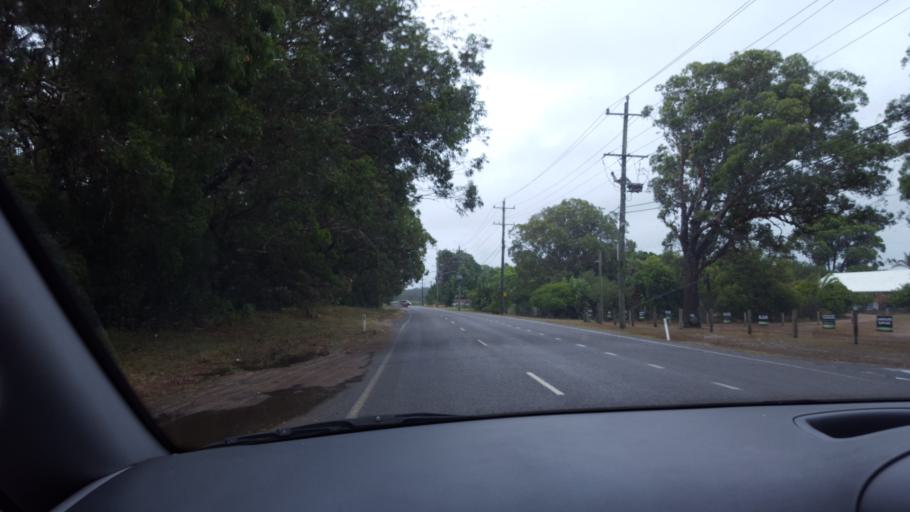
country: AU
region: New South Wales
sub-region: Port Stephens Shire
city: Anna Bay
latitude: -32.7724
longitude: 152.0767
